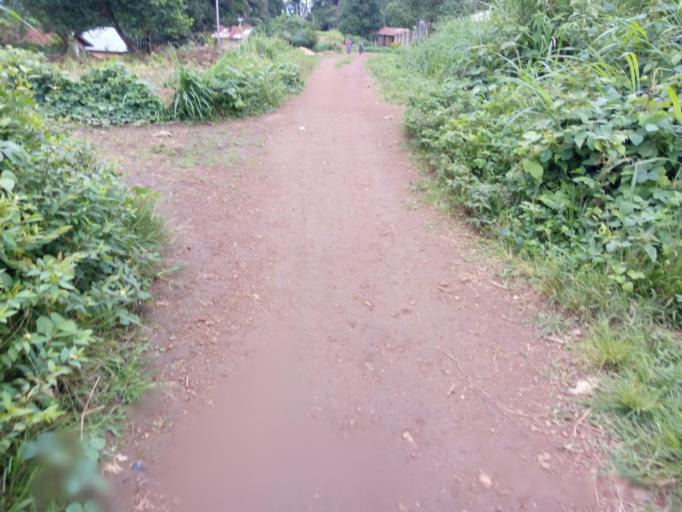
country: SL
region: Eastern Province
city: Buedu
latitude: 8.4544
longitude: -10.3317
